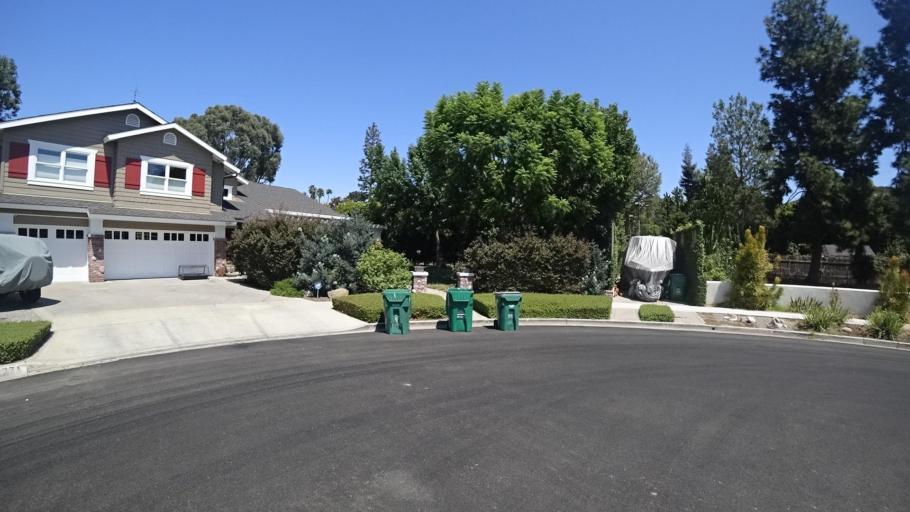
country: US
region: California
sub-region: Orange County
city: North Tustin
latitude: 33.7500
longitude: -117.7958
